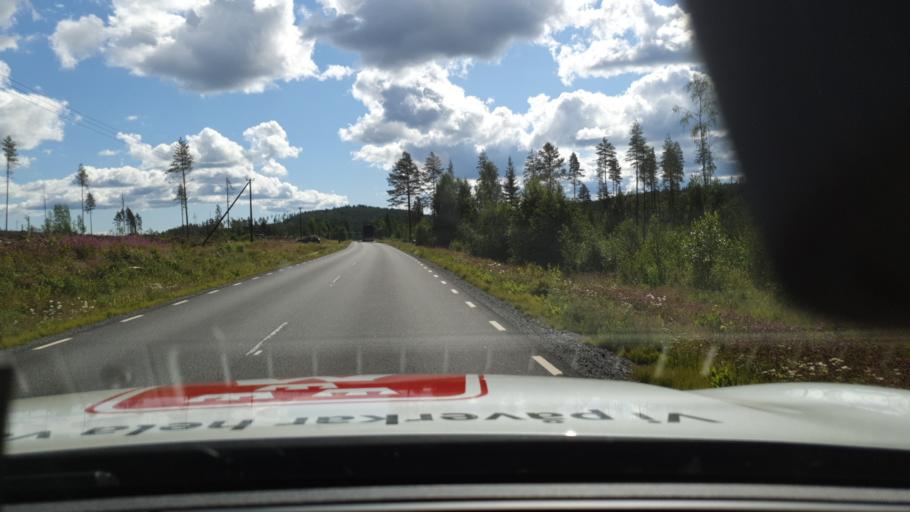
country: SE
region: Norrbotten
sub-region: Bodens Kommun
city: Saevast
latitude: 65.8346
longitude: 21.8621
